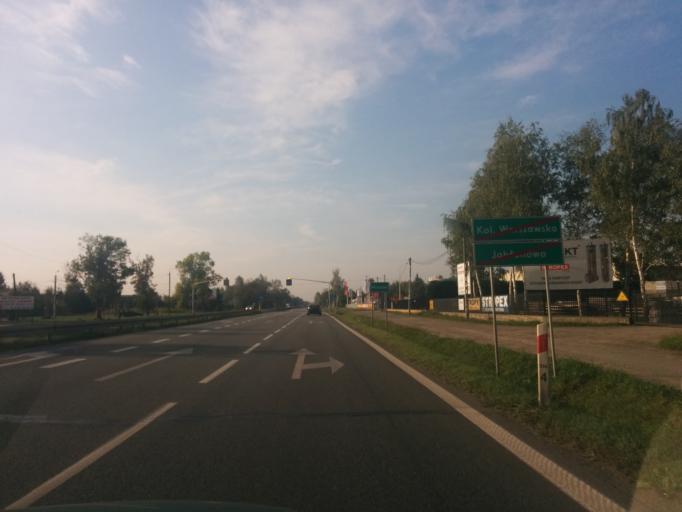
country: PL
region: Masovian Voivodeship
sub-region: Powiat piaseczynski
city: Tarczyn
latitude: 52.0482
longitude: 20.8648
